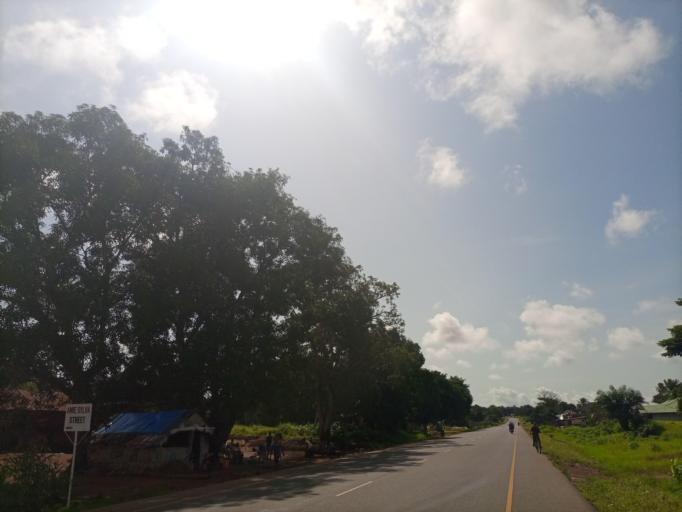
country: SL
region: Northern Province
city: Sawkta
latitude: 8.6315
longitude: -13.1826
